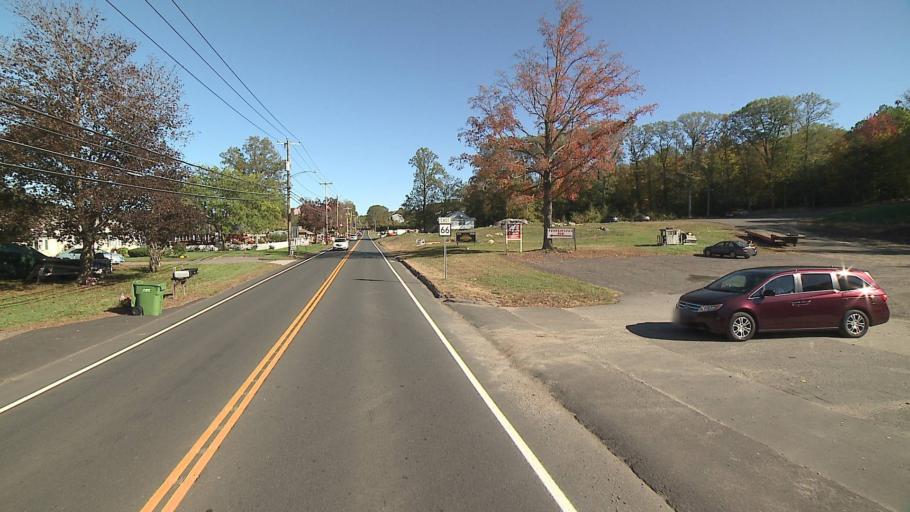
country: US
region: Connecticut
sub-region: Middlesex County
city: East Hampton
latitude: 41.5866
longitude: -72.4937
